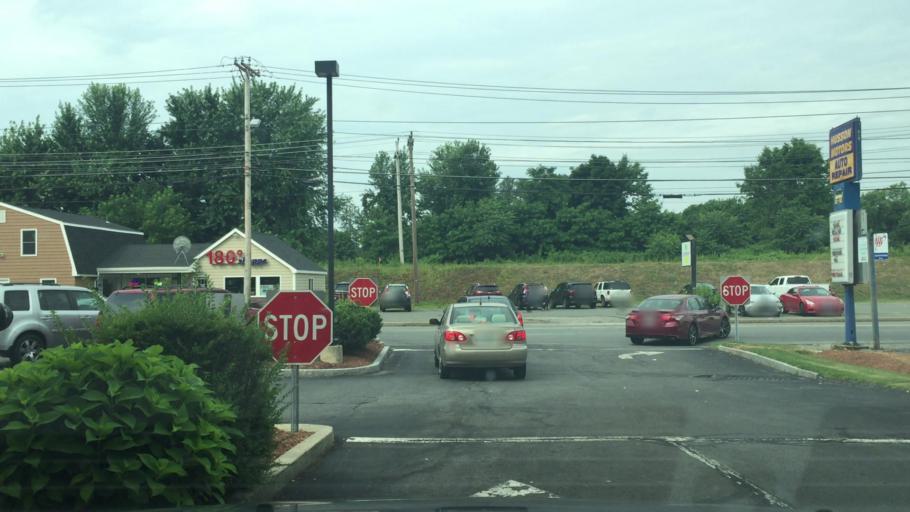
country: US
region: New Hampshire
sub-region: Rockingham County
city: Salem
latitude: 42.7777
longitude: -71.2266
